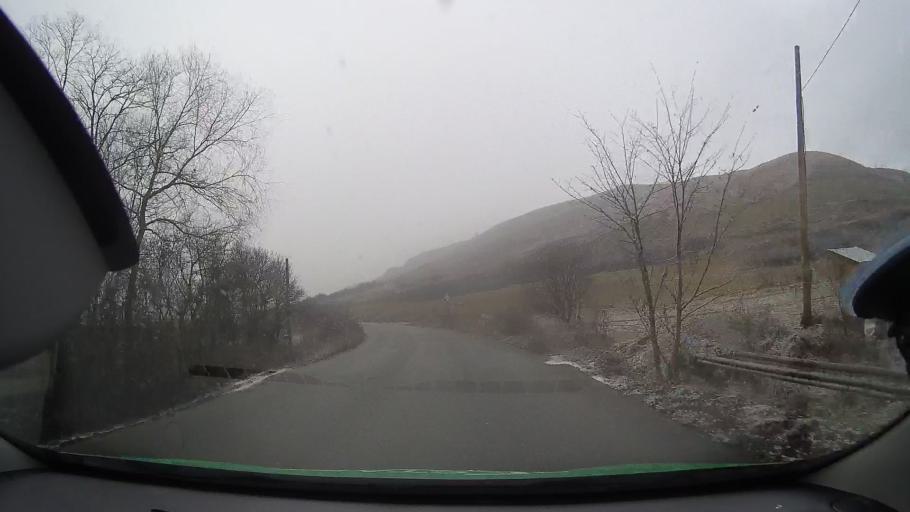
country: RO
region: Alba
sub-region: Comuna Noslac
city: Noslac
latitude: 46.3672
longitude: 23.9308
